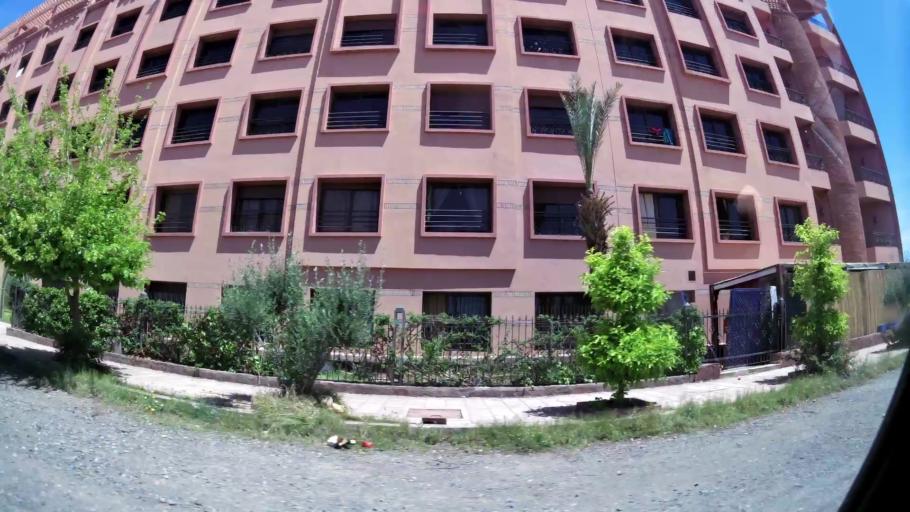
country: MA
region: Marrakech-Tensift-Al Haouz
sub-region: Marrakech
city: Marrakesh
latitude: 31.6204
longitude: -8.0141
